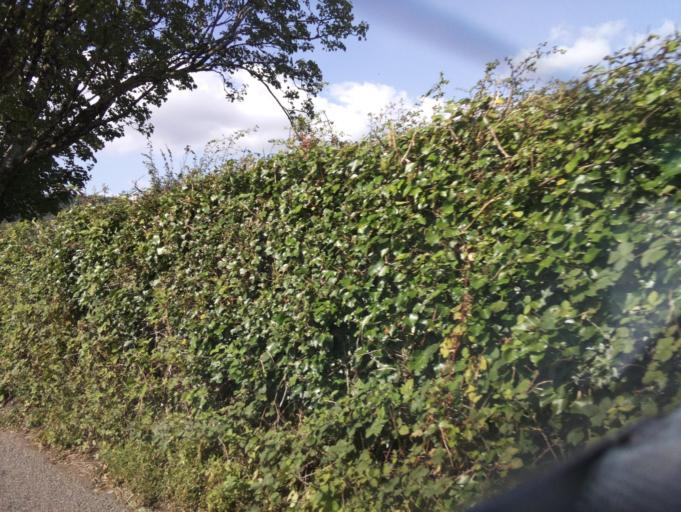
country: GB
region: England
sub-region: Devon
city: Ashburton
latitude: 50.5146
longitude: -3.7781
